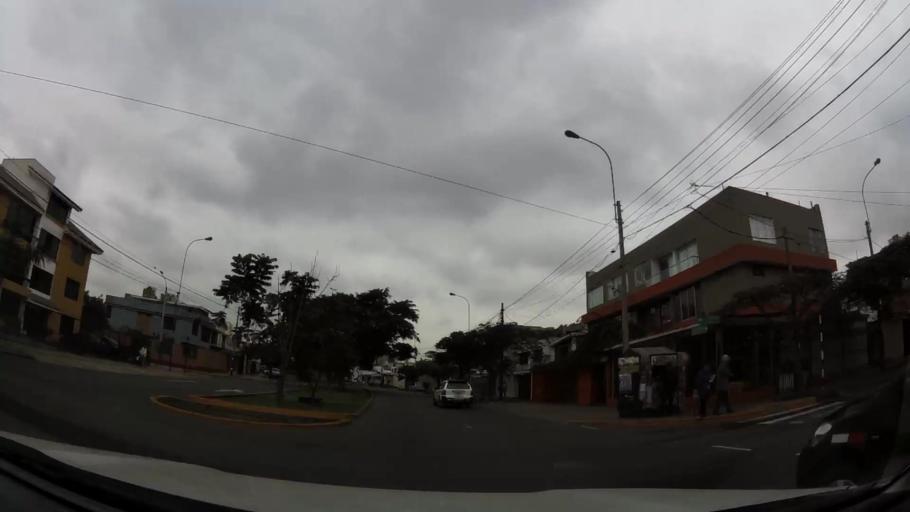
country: PE
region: Lima
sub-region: Lima
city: Surco
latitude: -12.1274
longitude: -76.9814
